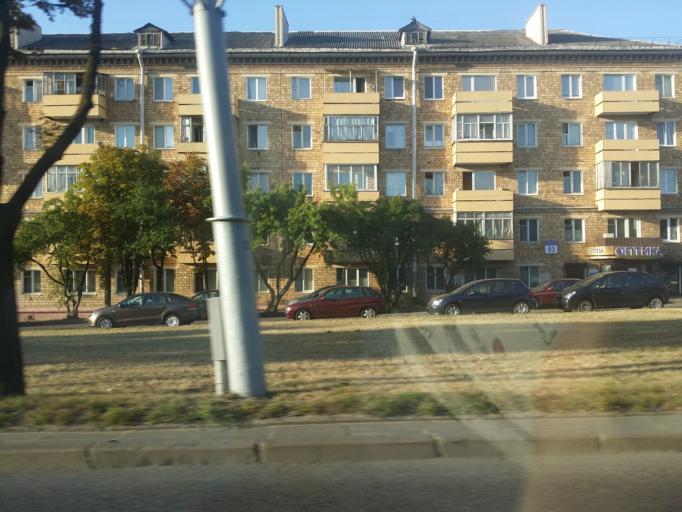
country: BY
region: Minsk
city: Minsk
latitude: 53.8736
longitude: 27.6356
